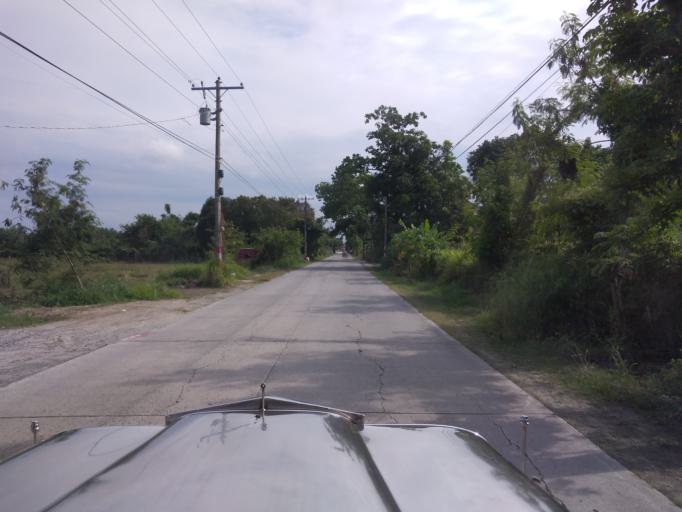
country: PH
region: Central Luzon
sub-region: Province of Pampanga
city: San Patricio
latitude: 15.0984
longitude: 120.7100
